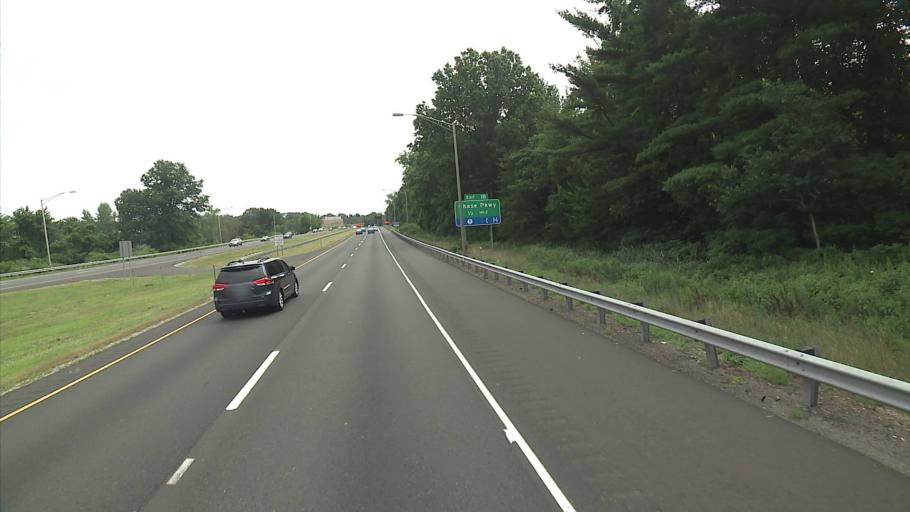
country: US
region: Connecticut
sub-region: New Haven County
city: Waterbury
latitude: 41.5440
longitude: -73.0736
